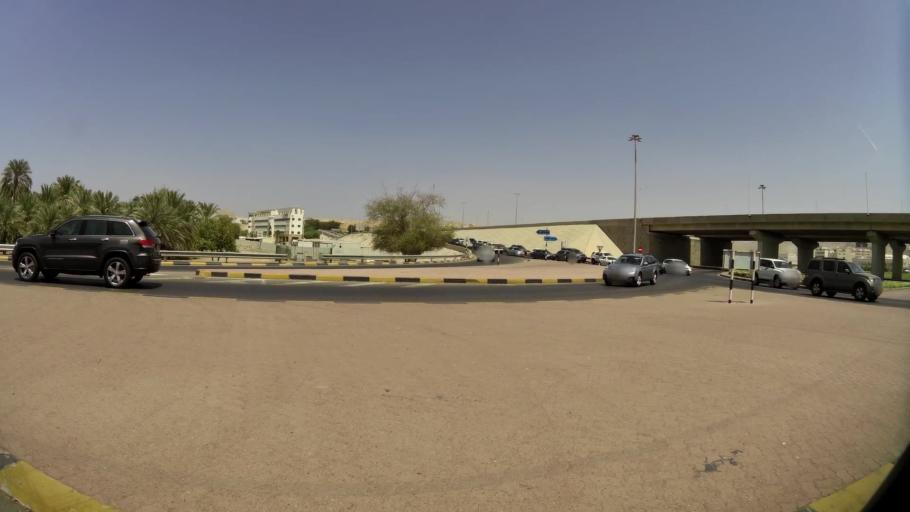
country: OM
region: Muhafazat Masqat
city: Muscat
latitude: 23.6174
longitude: 58.4948
